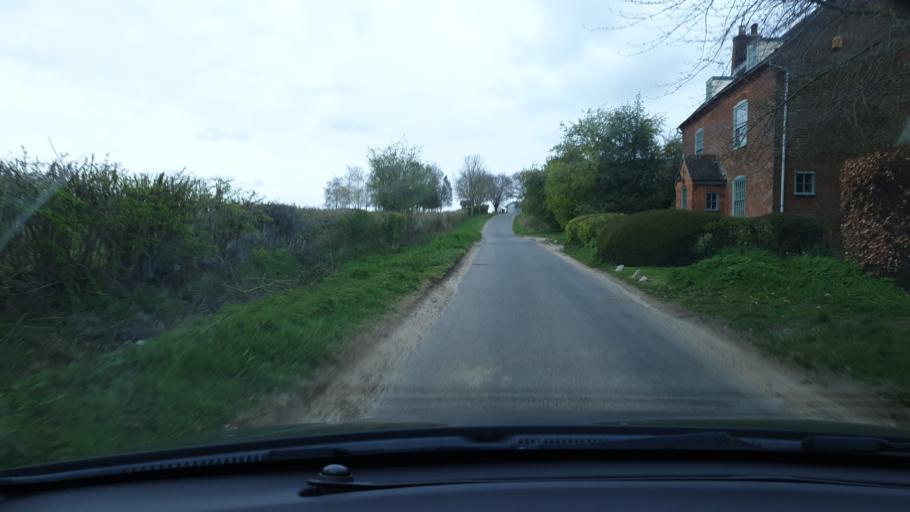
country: GB
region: England
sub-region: Essex
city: Mistley
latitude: 51.9415
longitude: 1.1570
